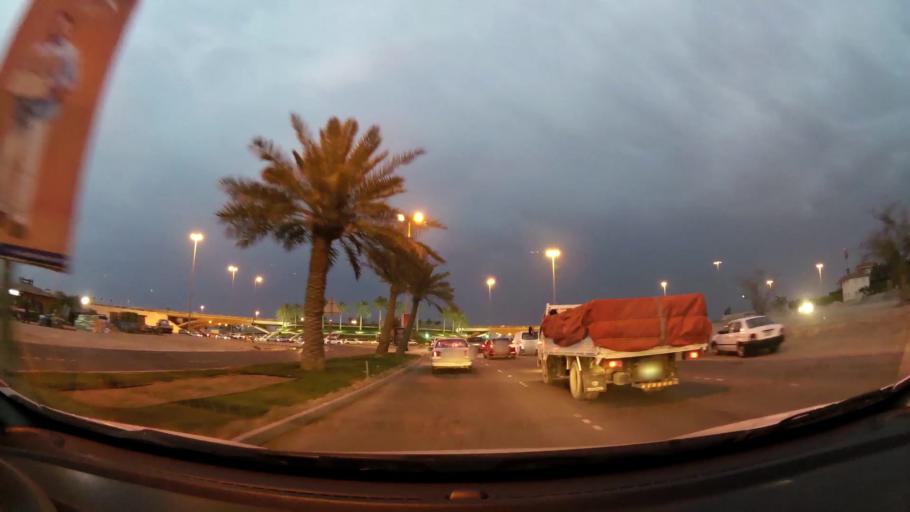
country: BH
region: Central Governorate
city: Madinat Hamad
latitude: 26.1396
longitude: 50.5087
